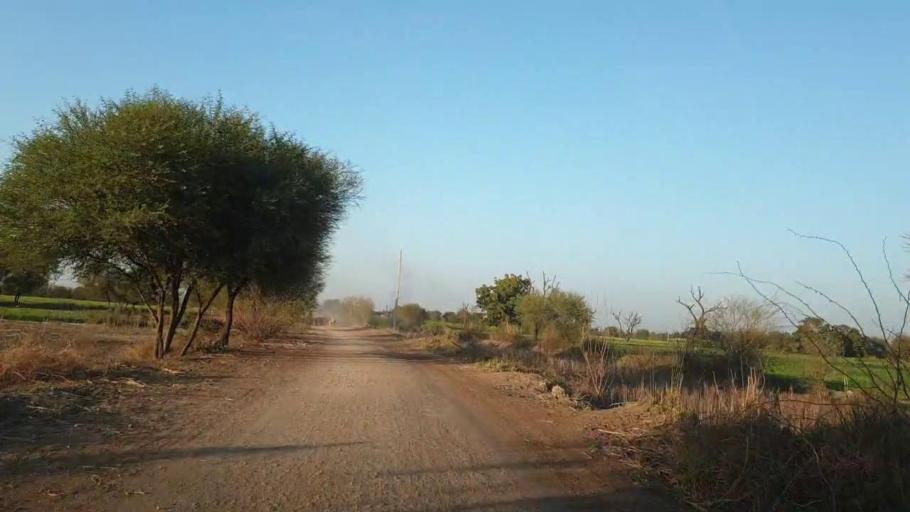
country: PK
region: Sindh
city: Mirpur Khas
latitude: 25.6915
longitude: 69.0508
